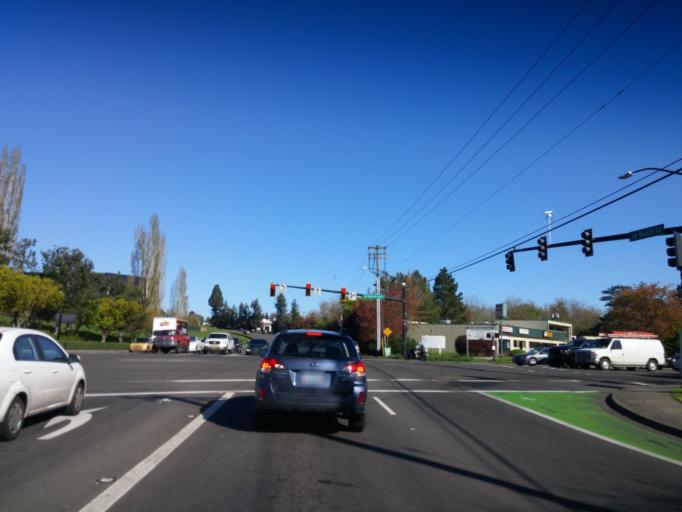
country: US
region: Oregon
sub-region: Washington County
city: Cedar Mill
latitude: 45.5104
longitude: -122.8219
